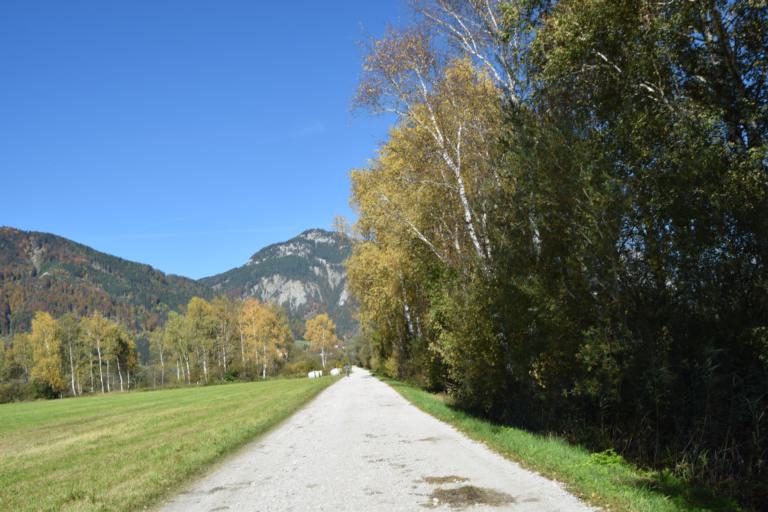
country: AT
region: Styria
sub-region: Politischer Bezirk Liezen
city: Irdning
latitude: 47.5191
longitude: 14.1052
